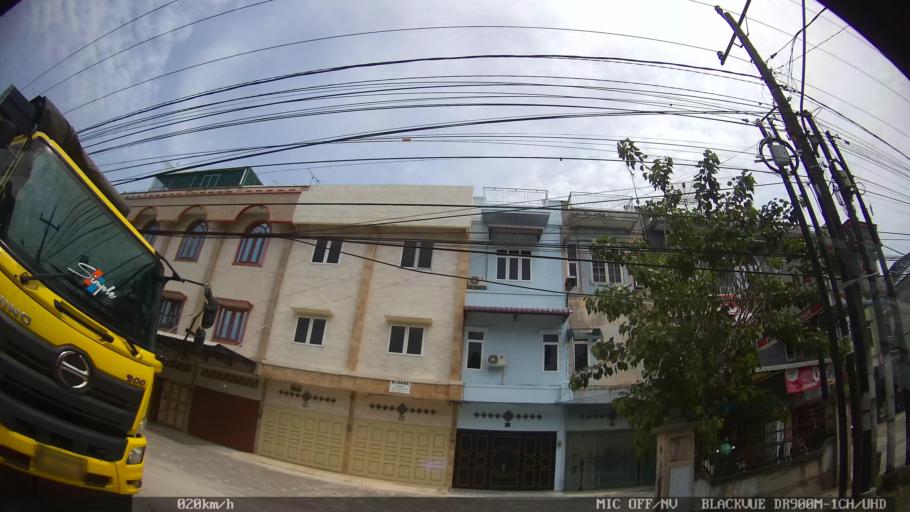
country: ID
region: North Sumatra
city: Sunggal
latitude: 3.5763
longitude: 98.6181
